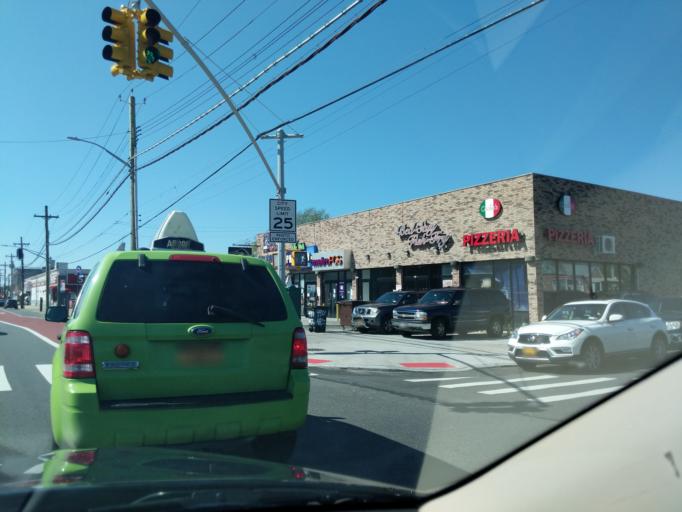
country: US
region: New York
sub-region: Kings County
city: Brooklyn
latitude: 40.6302
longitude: -73.9281
